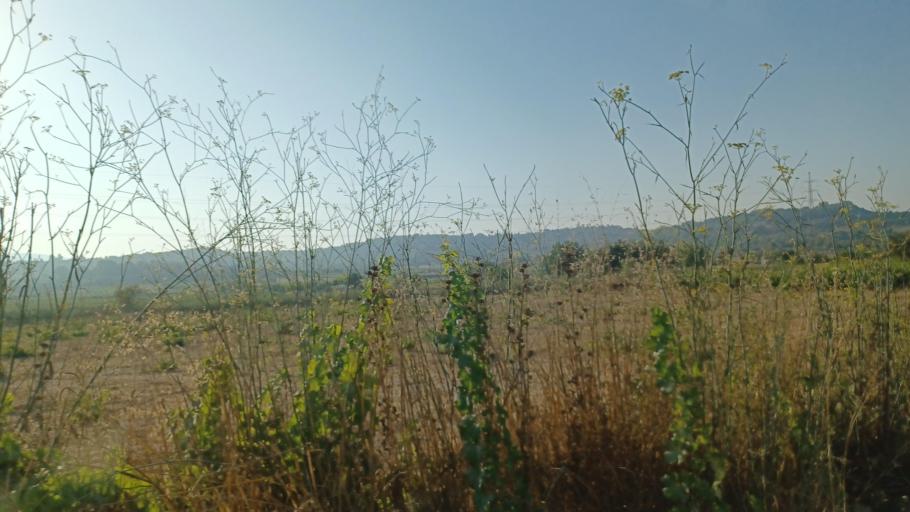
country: CY
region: Pafos
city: Tala
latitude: 34.8887
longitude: 32.4904
